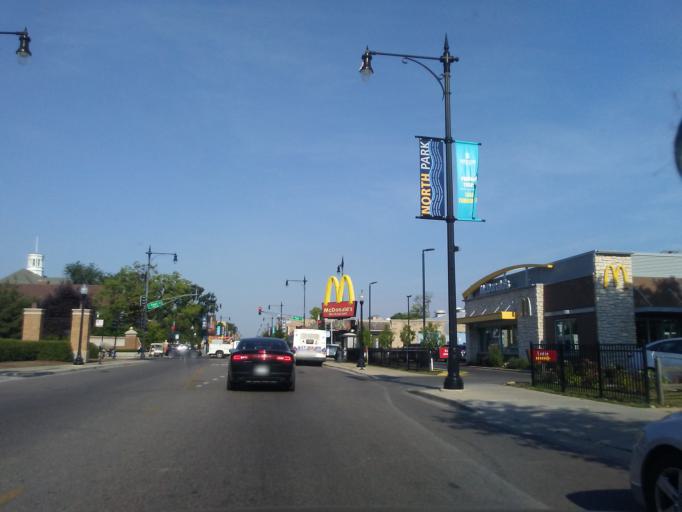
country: US
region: Illinois
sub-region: Cook County
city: Lincolnwood
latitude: 41.9758
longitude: -87.7078
